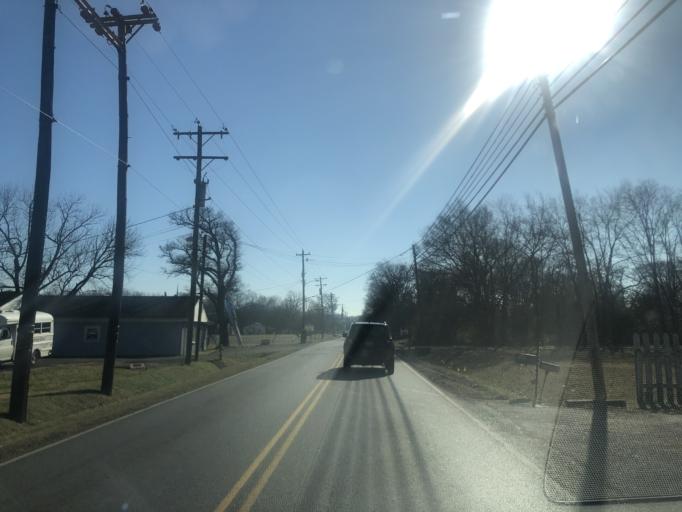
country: US
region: Tennessee
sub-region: Rutherford County
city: La Vergne
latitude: 36.0093
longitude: -86.5693
